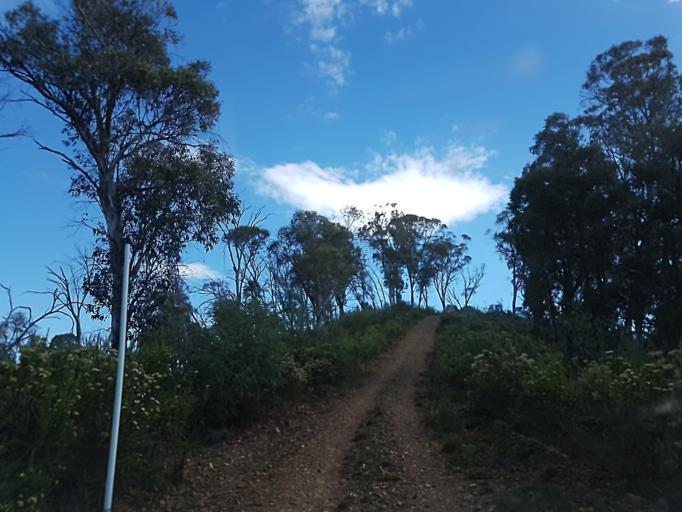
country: AU
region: Victoria
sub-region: Alpine
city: Mount Beauty
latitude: -36.9122
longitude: 147.0120
